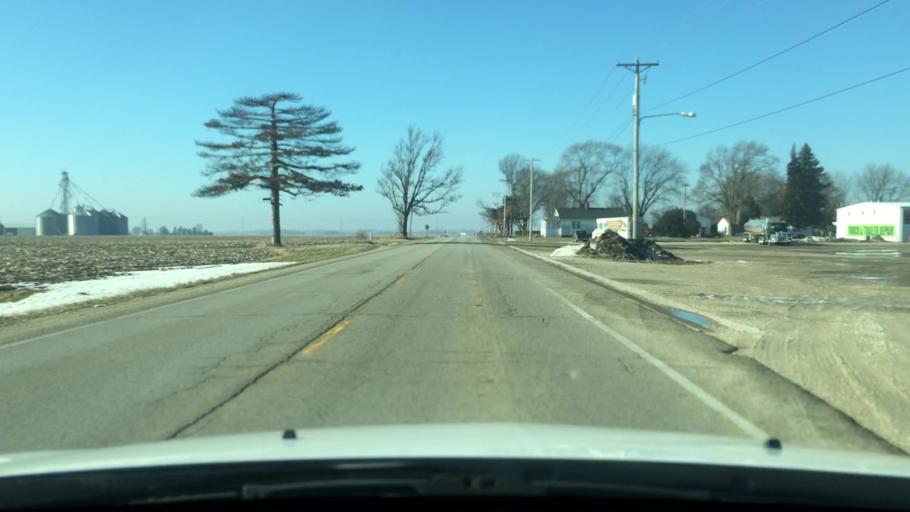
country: US
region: Illinois
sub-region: Ogle County
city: Rochelle
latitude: 41.8979
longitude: -89.0516
